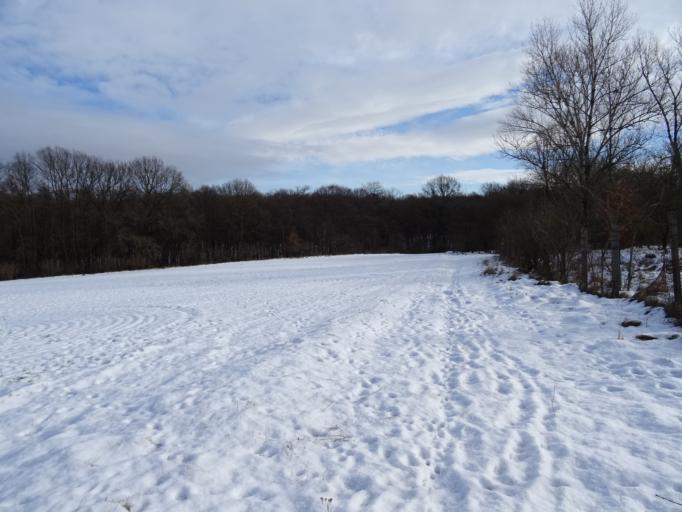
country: HU
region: Komarom-Esztergom
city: Oroszlany
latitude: 47.4919
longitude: 18.3427
